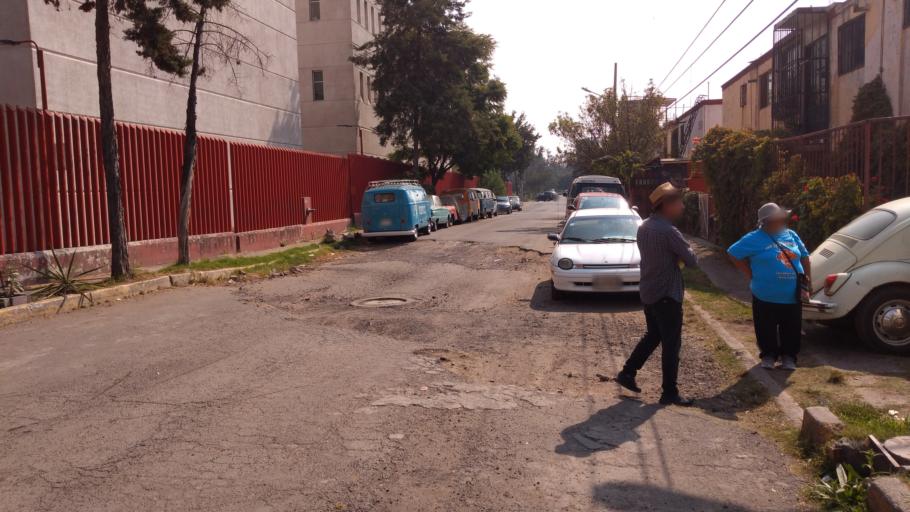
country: MX
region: Mexico City
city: Tlahuac
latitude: 19.2869
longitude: -99.0530
